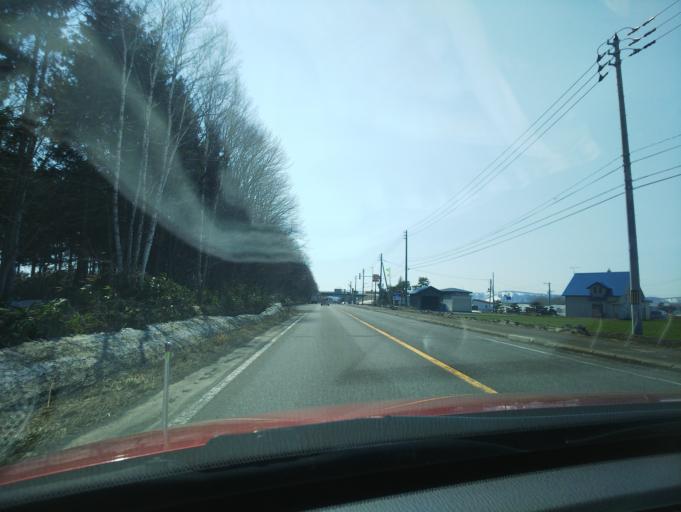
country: JP
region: Hokkaido
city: Nayoro
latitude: 44.3019
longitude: 142.4321
